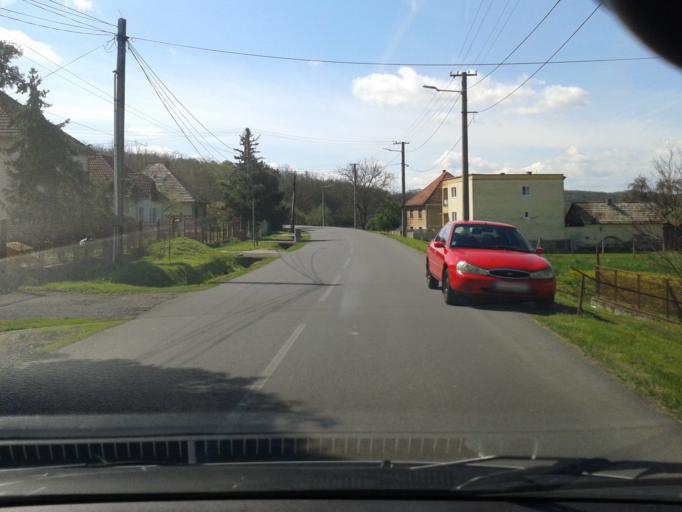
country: SK
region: Banskobystricky
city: Dudince
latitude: 48.1832
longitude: 18.8514
